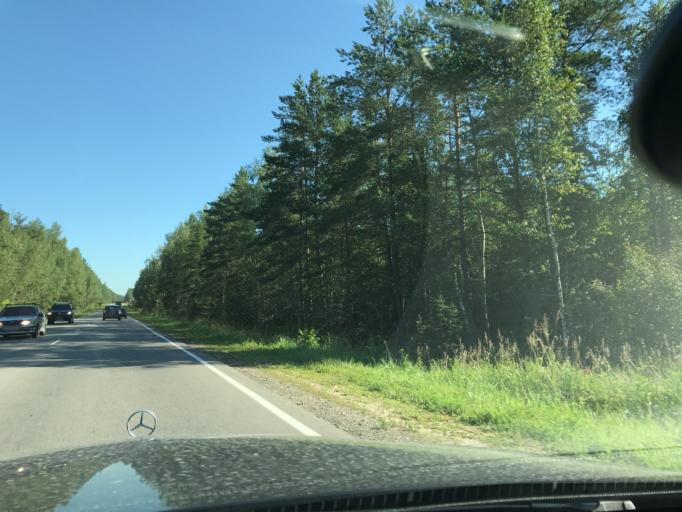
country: RU
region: Moskovskaya
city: Noginsk-9
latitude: 56.0852
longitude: 38.5777
